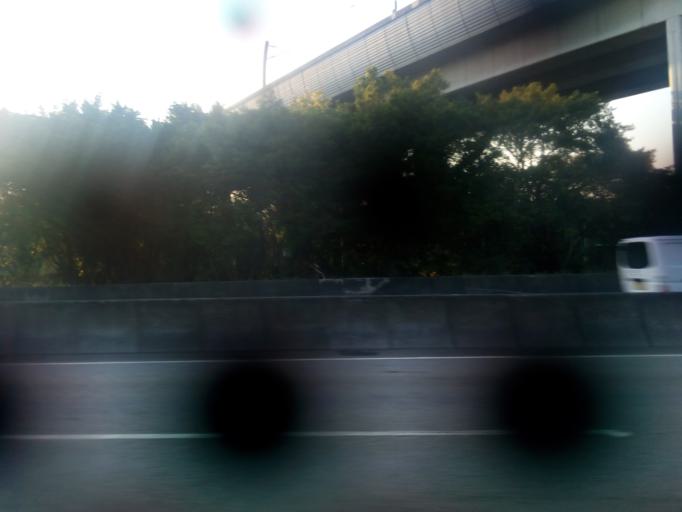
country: HK
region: Yuen Long
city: Yuen Long Kau Hui
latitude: 22.4438
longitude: 113.9993
